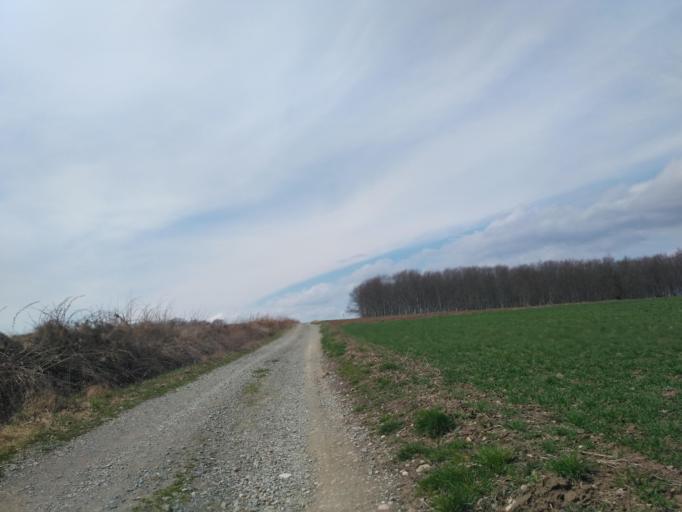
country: PL
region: Subcarpathian Voivodeship
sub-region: Powiat ropczycko-sedziszowski
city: Iwierzyce
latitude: 50.0395
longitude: 21.7314
